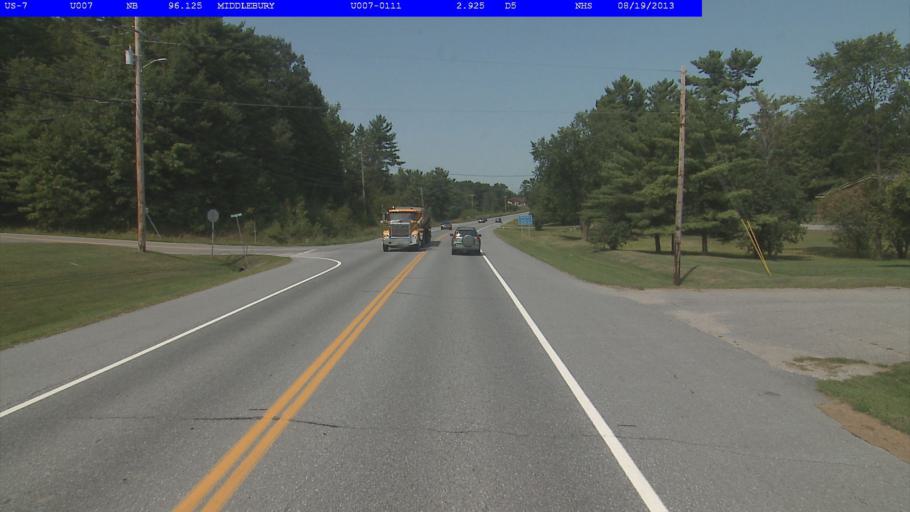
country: US
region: Vermont
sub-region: Addison County
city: Middlebury (village)
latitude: 43.9913
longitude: -73.1399
